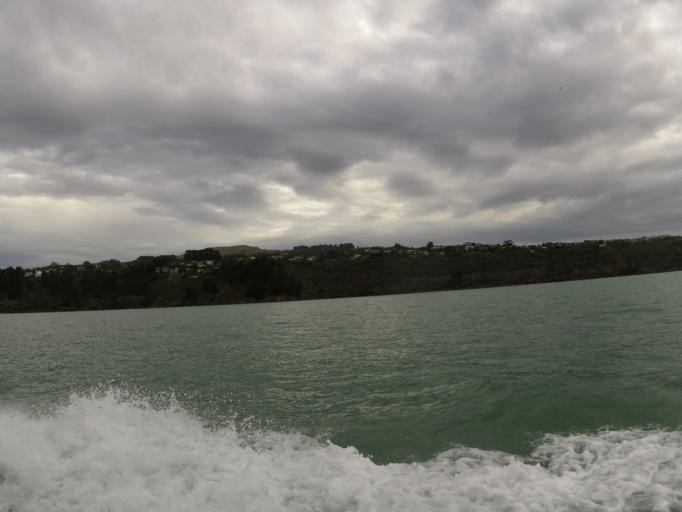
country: NZ
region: Canterbury
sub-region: Christchurch City
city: Christchurch
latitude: -43.6203
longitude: 172.7309
